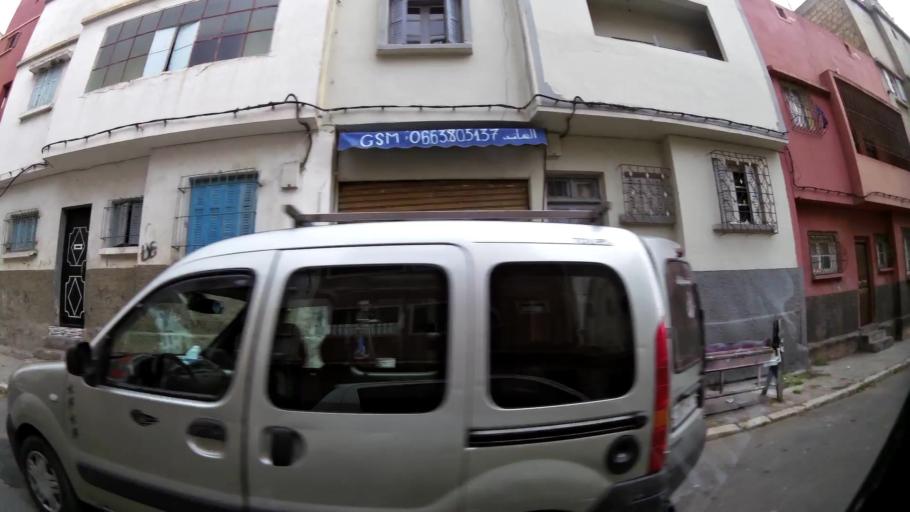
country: MA
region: Grand Casablanca
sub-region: Casablanca
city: Casablanca
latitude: 33.5657
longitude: -7.5622
